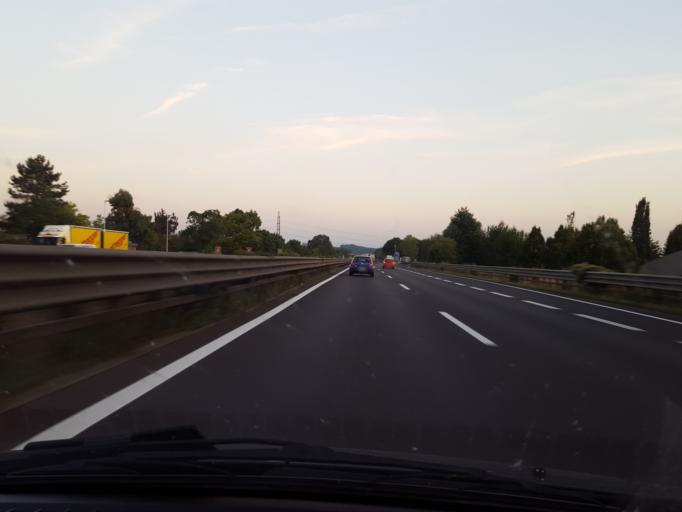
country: AT
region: Upper Austria
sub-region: Politischer Bezirk Linz-Land
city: Ansfelden
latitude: 48.2470
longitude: 14.2973
